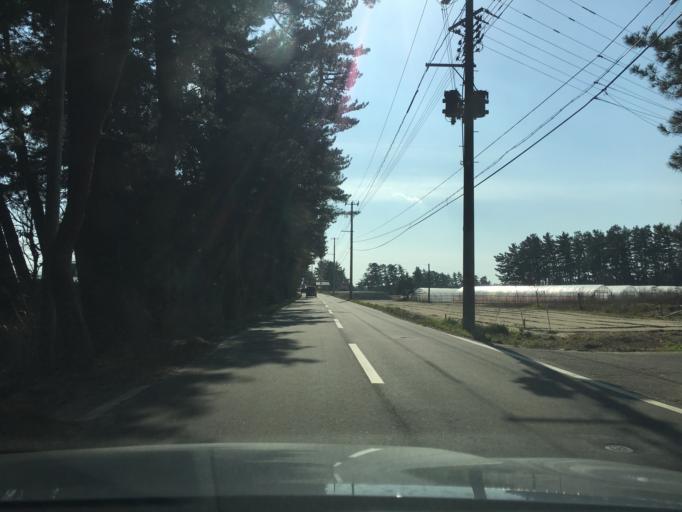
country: JP
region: Yamagata
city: Tsuruoka
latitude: 38.8062
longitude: 139.7766
